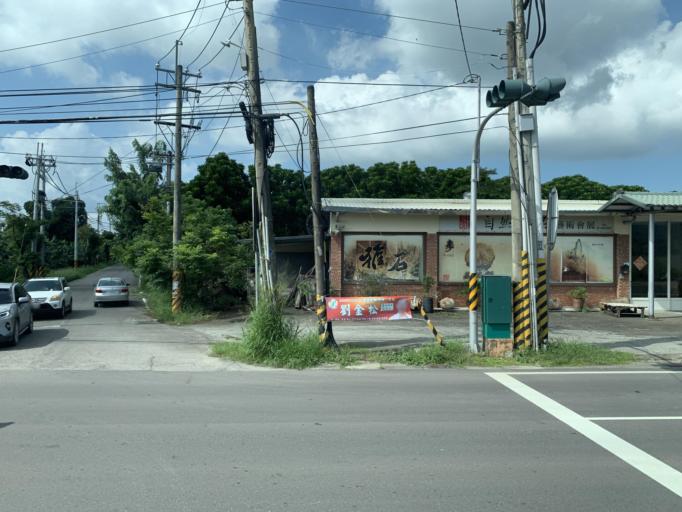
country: TW
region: Taiwan
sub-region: Pingtung
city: Pingtung
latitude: 22.8772
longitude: 120.4971
